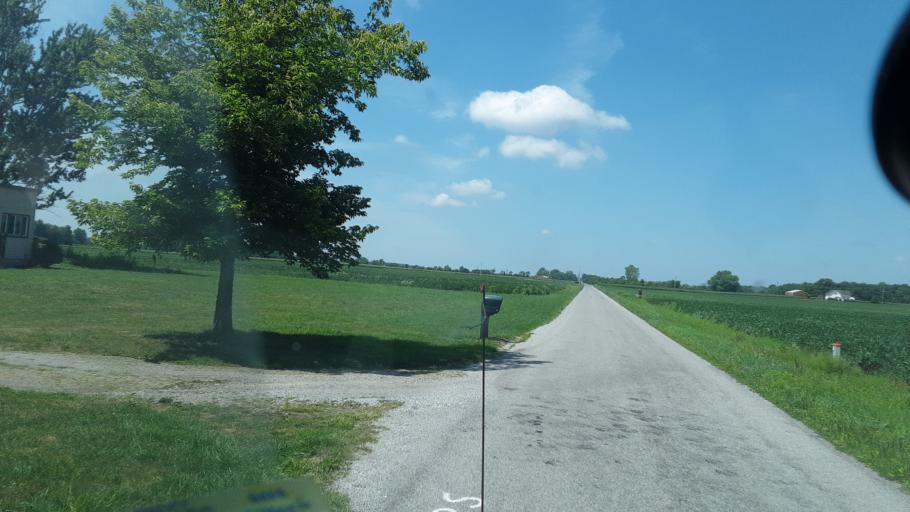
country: US
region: Ohio
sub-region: Hancock County
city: Findlay
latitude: 40.9715
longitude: -83.5684
